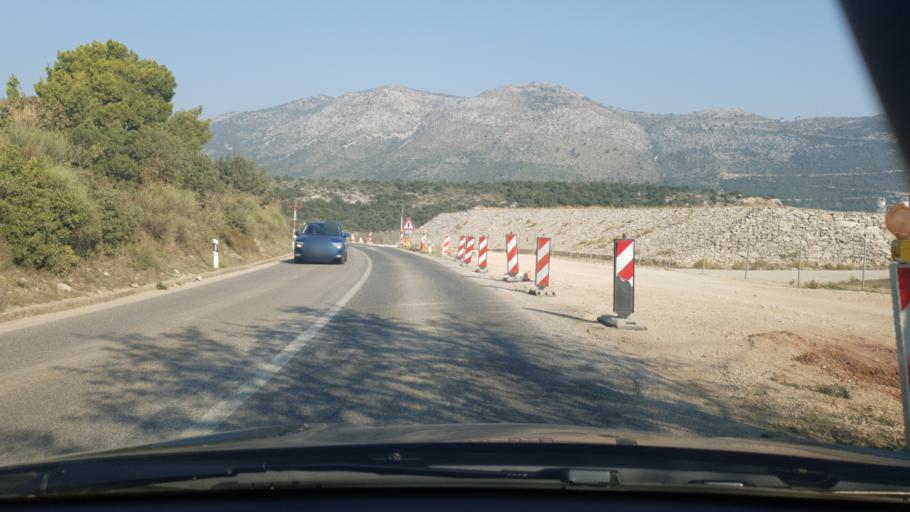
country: HR
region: Dubrovacko-Neretvanska
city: Cavtat
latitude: 42.5690
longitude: 18.2454
